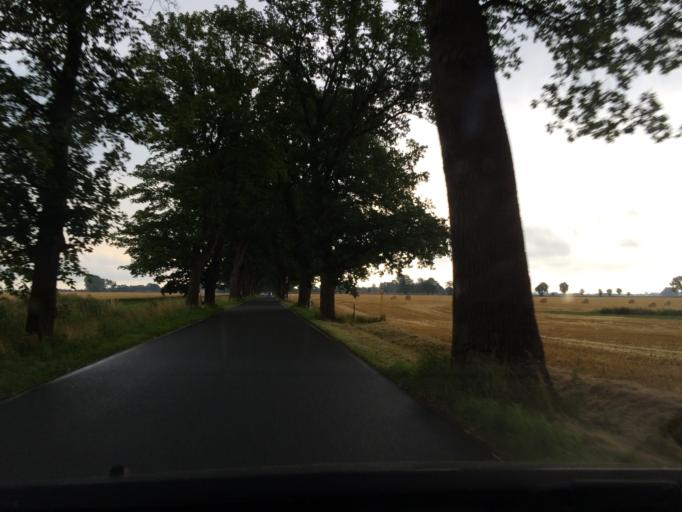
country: DE
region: Mecklenburg-Vorpommern
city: Preetz
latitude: 54.3496
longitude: 12.9937
